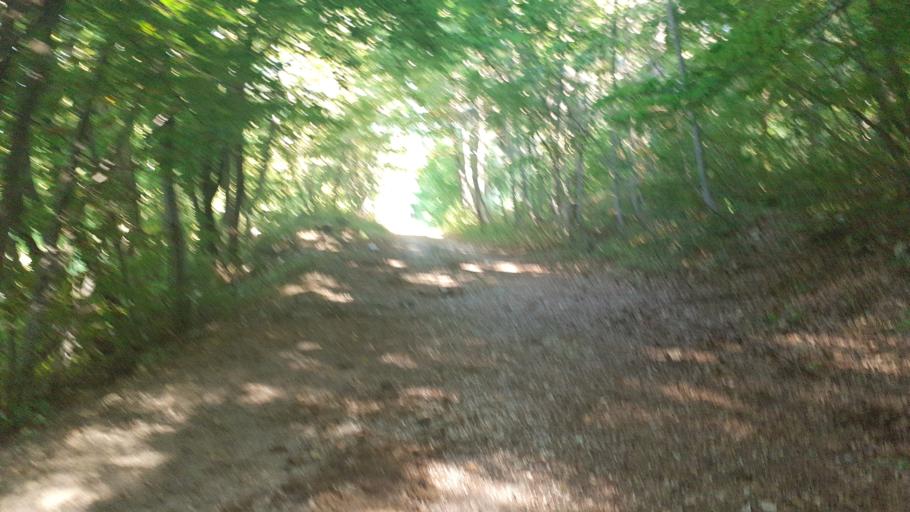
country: IT
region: Abruzzo
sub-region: Provincia di Pescara
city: Sant'Eufemia a Maiella
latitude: 42.1050
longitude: 14.0054
